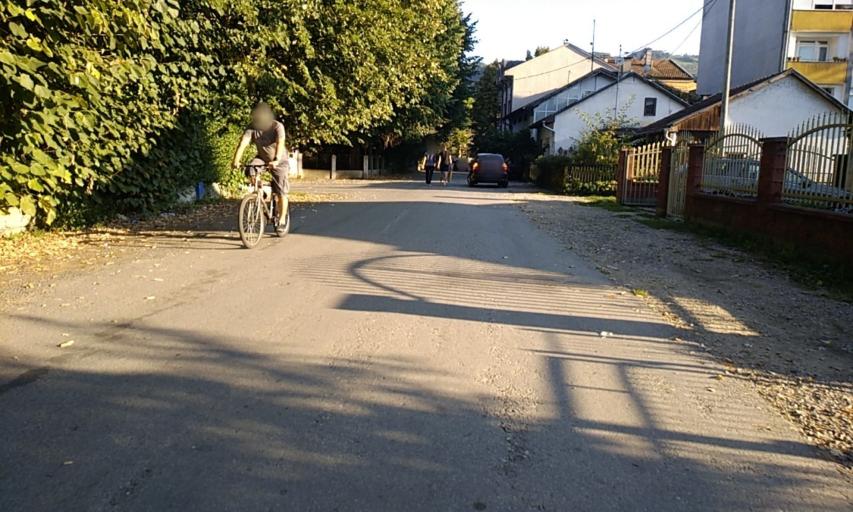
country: BA
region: Republika Srpska
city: Mejdan - Obilicevo
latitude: 44.7652
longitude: 17.1956
